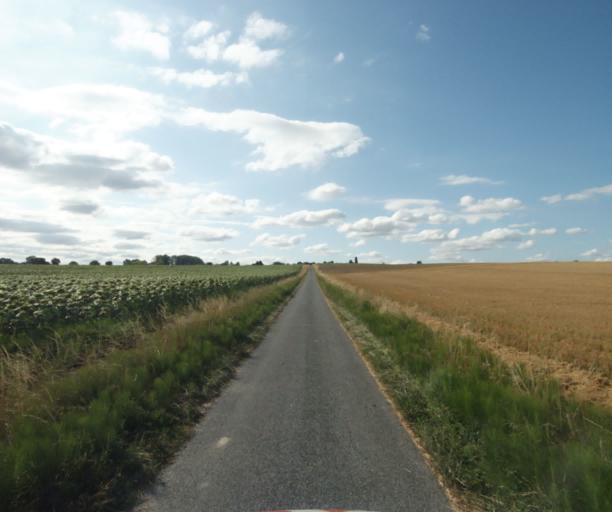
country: FR
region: Midi-Pyrenees
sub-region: Departement du Tarn
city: Puylaurens
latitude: 43.5264
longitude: 1.9971
